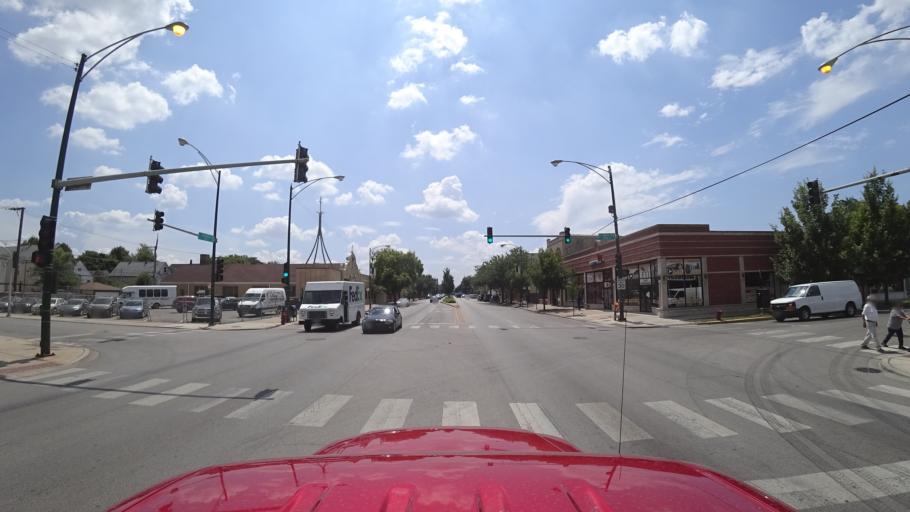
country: US
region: Illinois
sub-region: Cook County
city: Chicago
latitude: 41.8124
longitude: -87.6651
